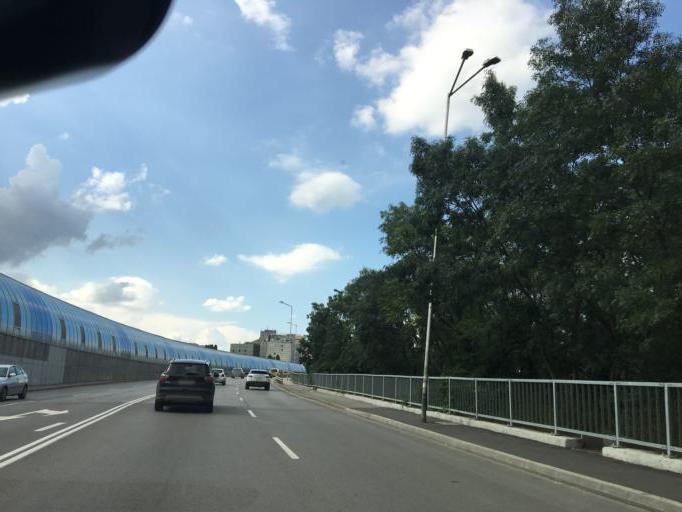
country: BG
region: Sofia-Capital
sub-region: Stolichna Obshtina
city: Sofia
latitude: 42.6662
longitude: 23.3543
